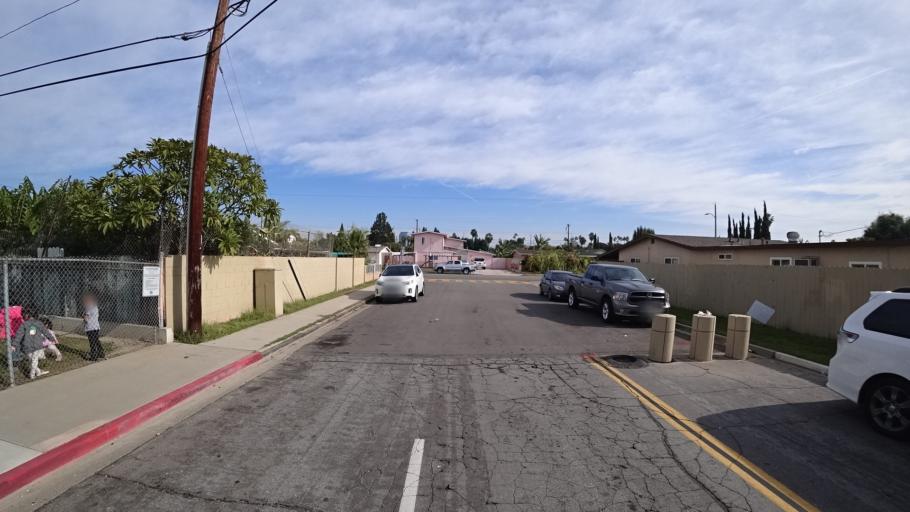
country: US
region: California
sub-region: Orange County
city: Garden Grove
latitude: 33.7854
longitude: -117.9095
